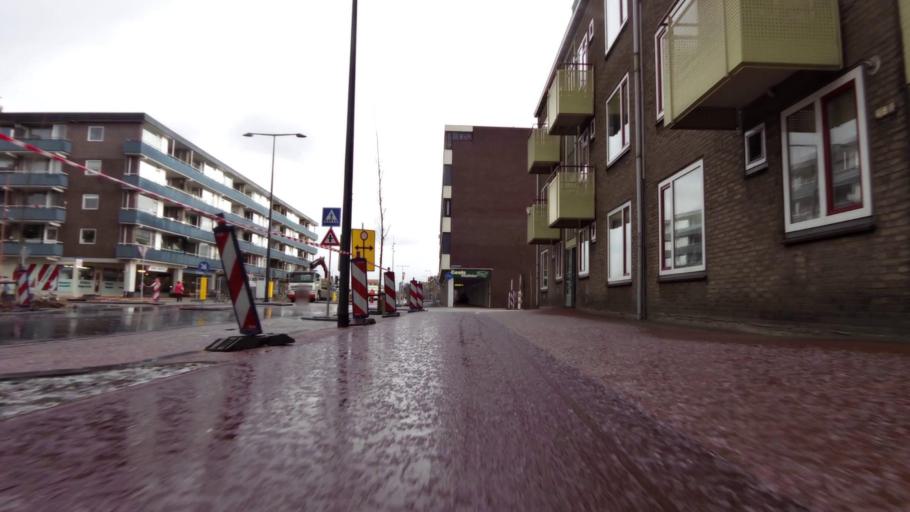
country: NL
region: North Holland
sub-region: Gemeente Velsen
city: Velsen-Zuid
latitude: 52.4572
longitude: 4.6105
